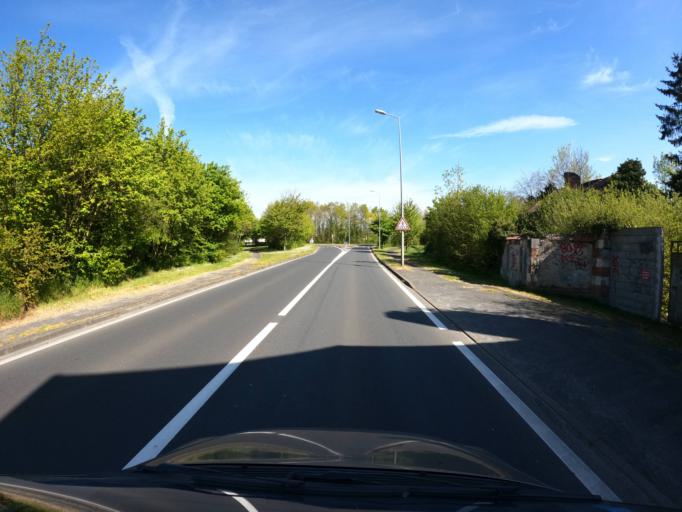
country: FR
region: Pays de la Loire
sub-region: Departement de Maine-et-Loire
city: Cholet
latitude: 47.0687
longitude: -0.9062
